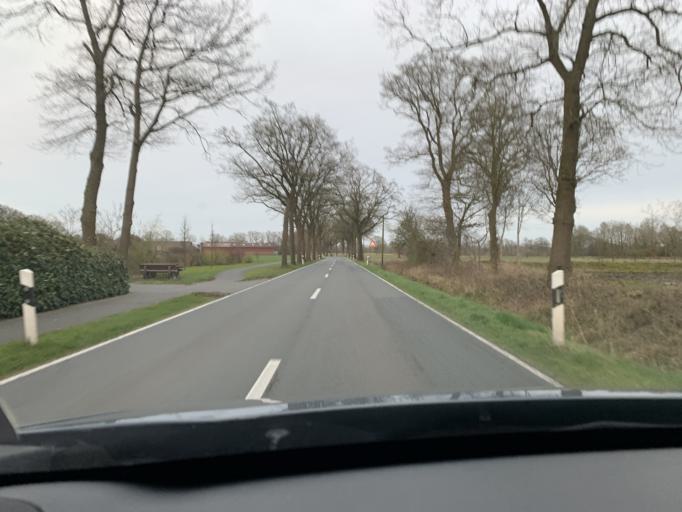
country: DE
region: Lower Saxony
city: Apen
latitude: 53.1770
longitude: 7.8058
